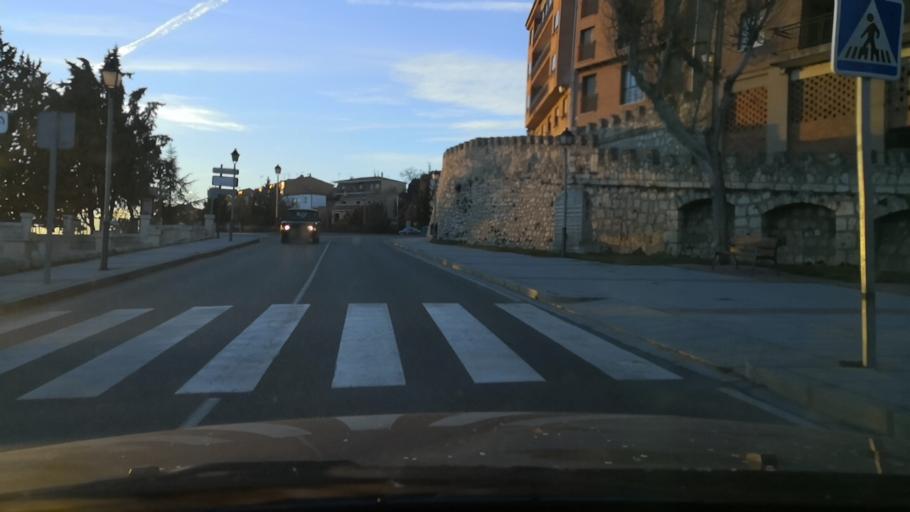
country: ES
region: Castille and Leon
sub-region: Provincia de Valladolid
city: Tordesillas
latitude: 41.4993
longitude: -5.0016
